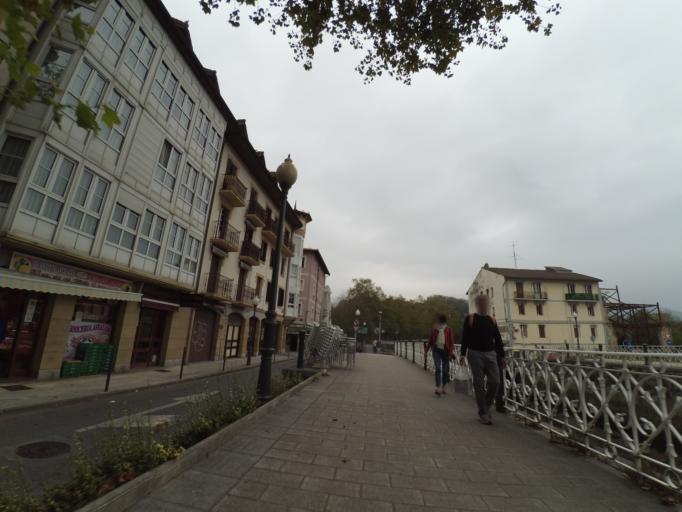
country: ES
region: Basque Country
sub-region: Provincia de Guipuzcoa
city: Irun
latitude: 43.3387
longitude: -1.7842
